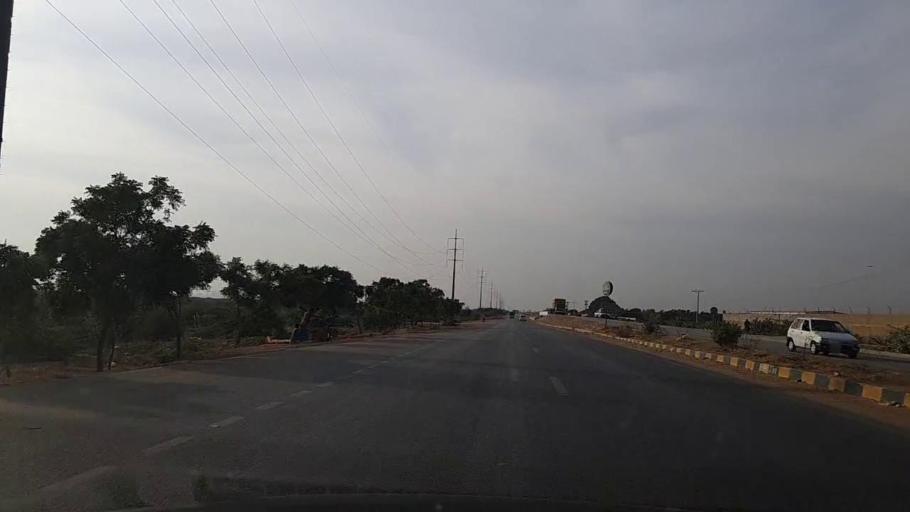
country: PK
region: Sindh
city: Gharo
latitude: 24.8288
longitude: 67.4679
